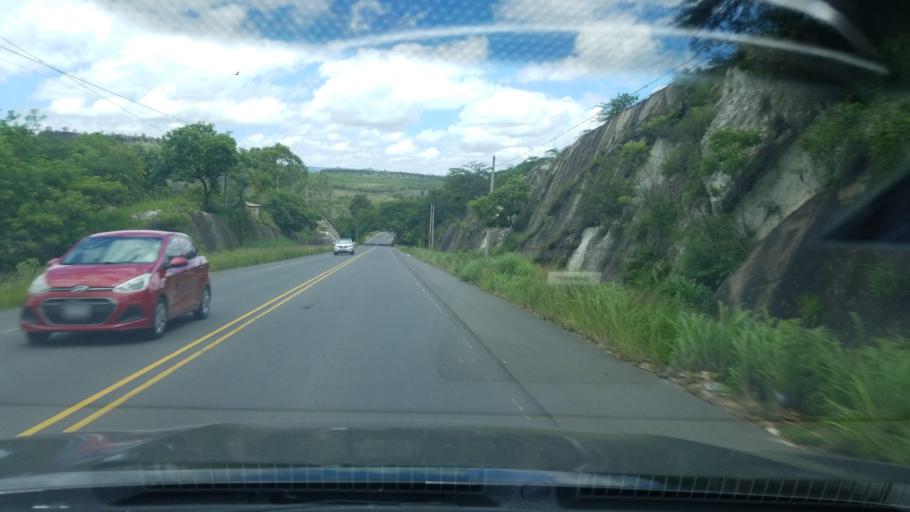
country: HN
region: Francisco Morazan
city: Cofradia
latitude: 14.3109
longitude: -87.2168
